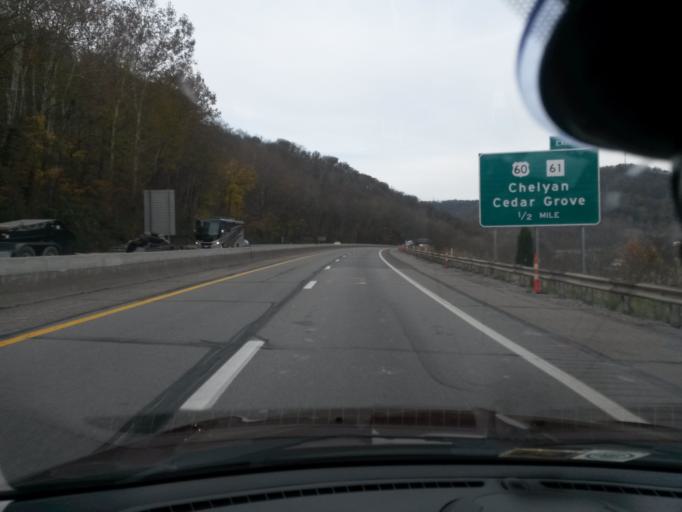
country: US
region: West Virginia
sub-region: Kanawha County
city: Chesapeake
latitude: 38.1933
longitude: -81.4884
